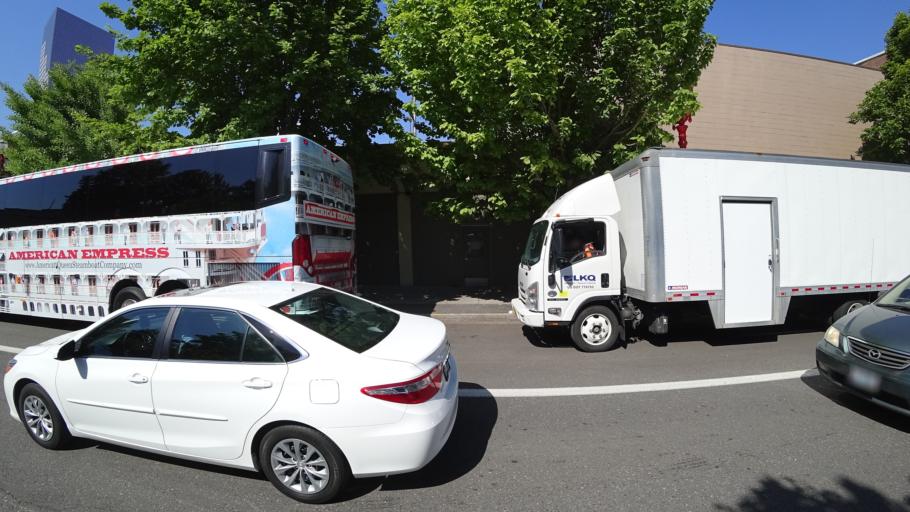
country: US
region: Oregon
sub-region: Multnomah County
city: Portland
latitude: 45.5255
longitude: -122.6735
